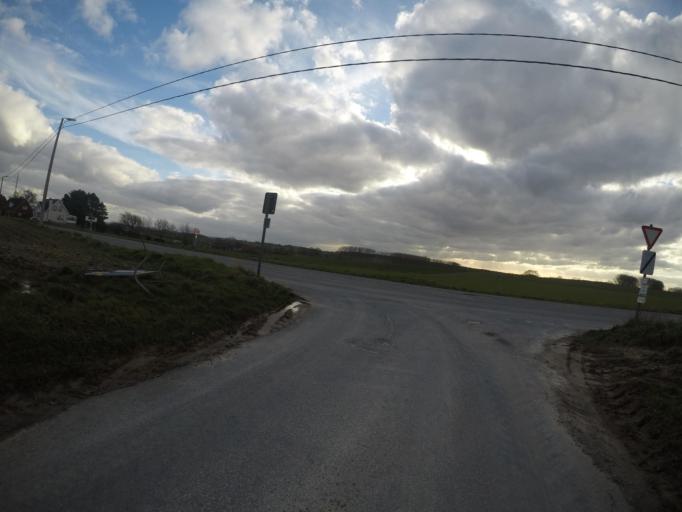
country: BE
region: Flanders
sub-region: Provincie Vlaams-Brabant
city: Pepingen
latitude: 50.7294
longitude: 4.1224
